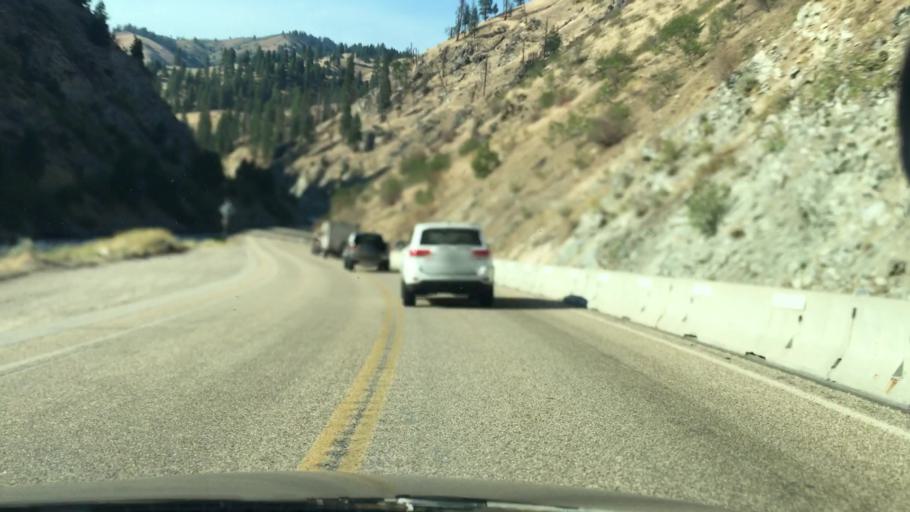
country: US
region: Idaho
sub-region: Boise County
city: Idaho City
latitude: 44.1000
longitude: -116.0954
